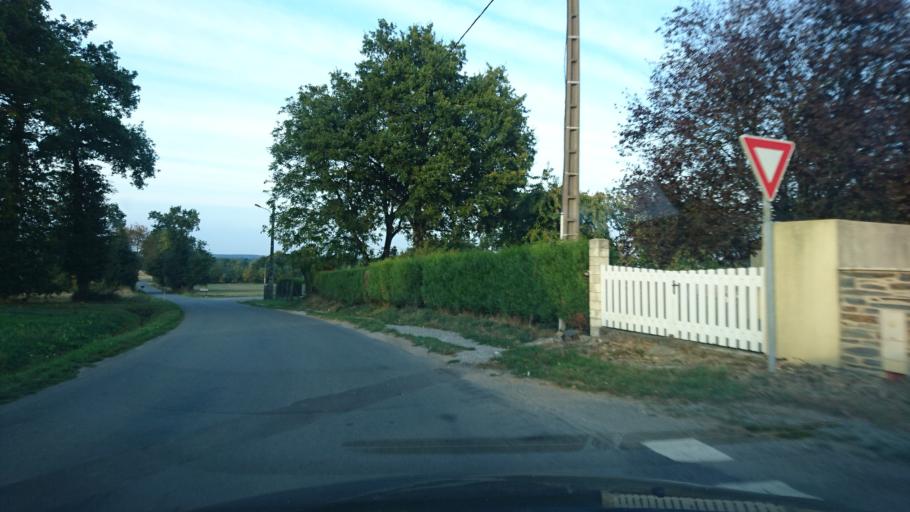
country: FR
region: Brittany
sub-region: Departement d'Ille-et-Vilaine
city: Sixt-sur-Aff
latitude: 47.7779
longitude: -2.0749
